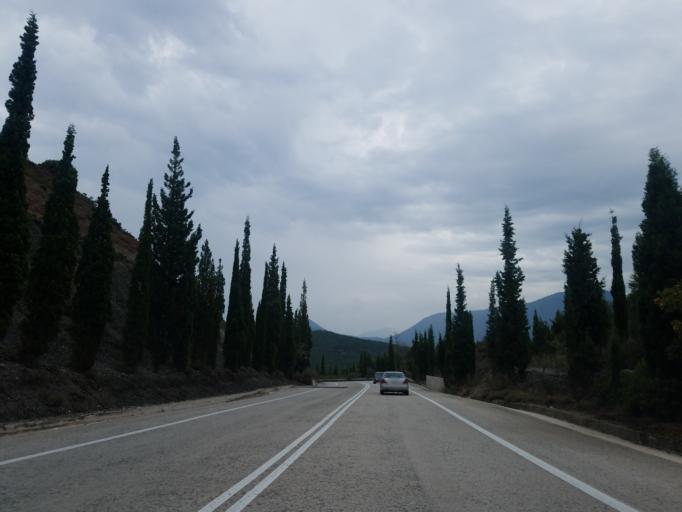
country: GR
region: Central Greece
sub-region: Nomos Voiotias
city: Livadeia
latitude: 38.4424
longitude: 22.8077
